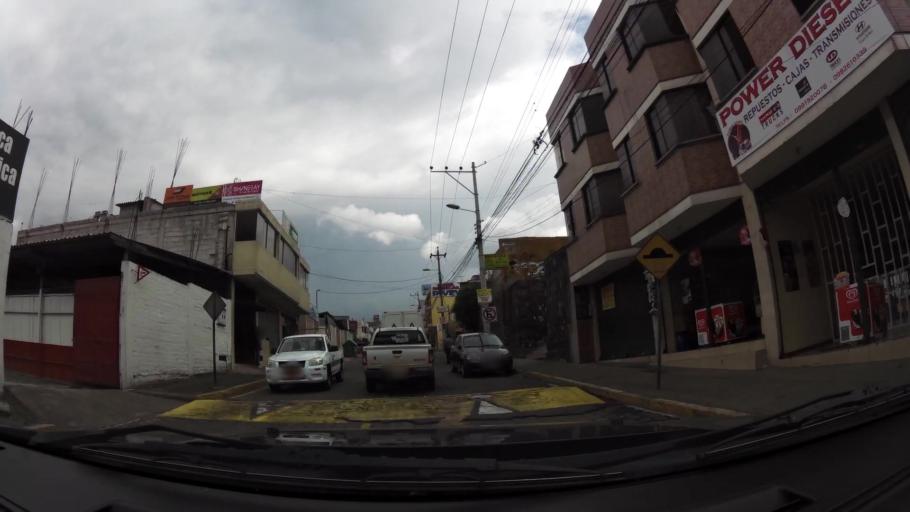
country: EC
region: Pichincha
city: Sangolqui
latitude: -0.3307
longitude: -78.4516
